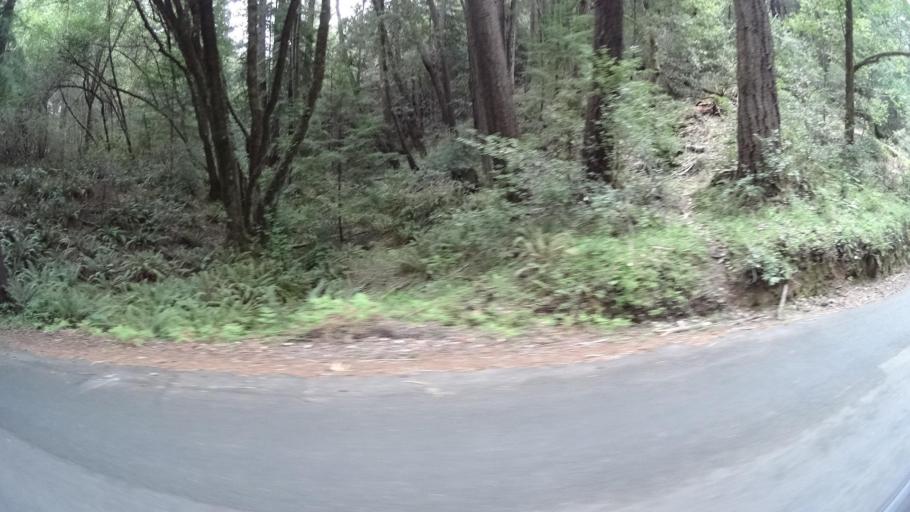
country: US
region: California
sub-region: Humboldt County
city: Redway
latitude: 40.0012
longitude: -123.9284
